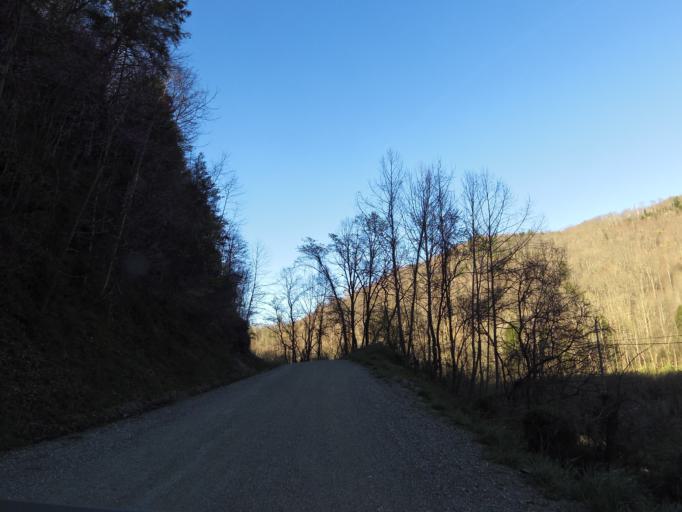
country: US
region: Tennessee
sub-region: Campbell County
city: Caryville
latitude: 36.2613
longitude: -84.3940
